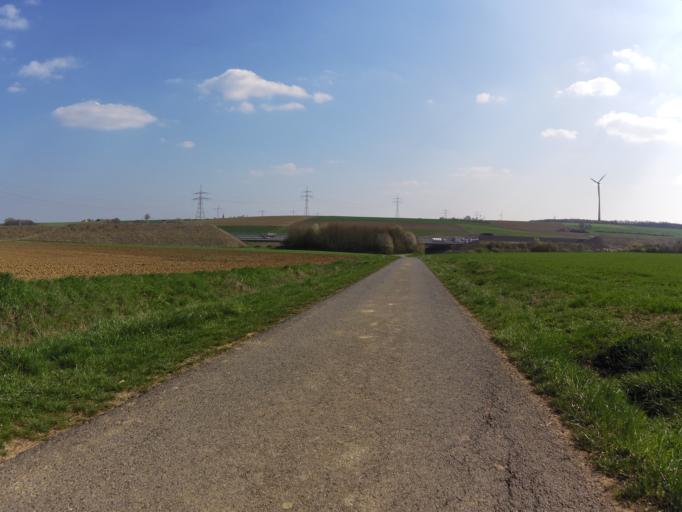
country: DE
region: Bavaria
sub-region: Regierungsbezirk Unterfranken
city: Theilheim
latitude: 49.7592
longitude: 10.0476
